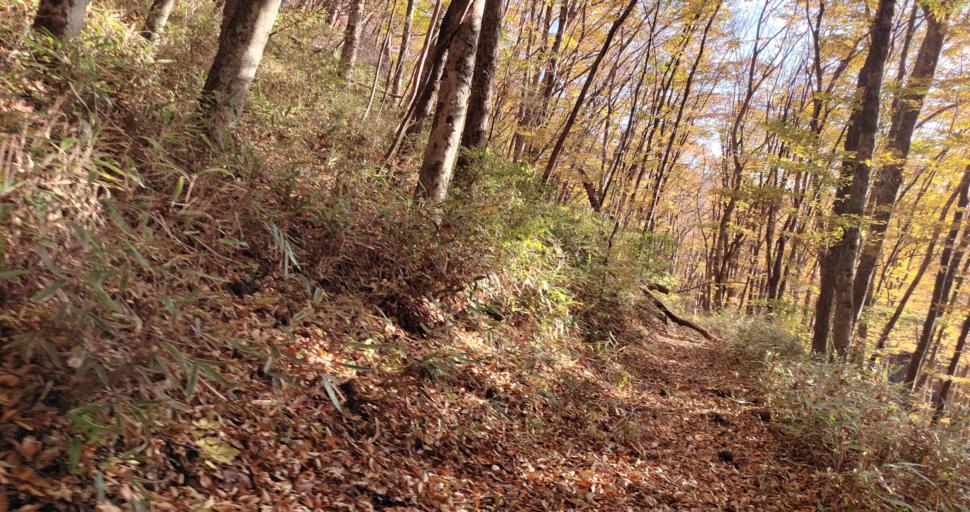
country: JP
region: Nagano
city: Komoro
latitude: 36.3881
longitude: 138.4385
